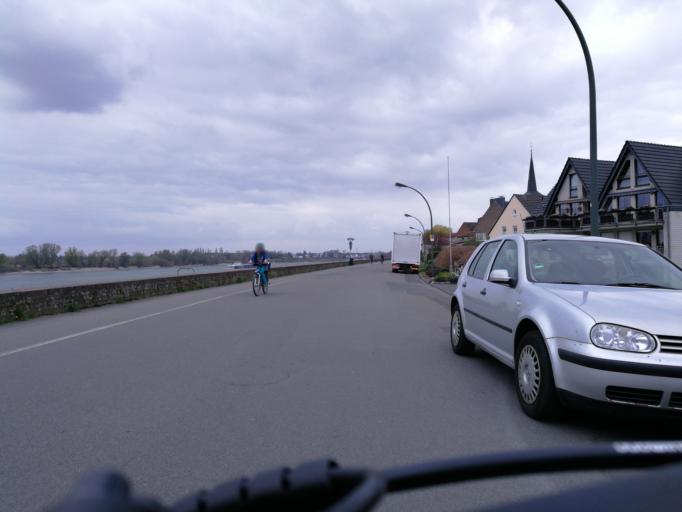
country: DE
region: North Rhine-Westphalia
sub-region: Regierungsbezirk Dusseldorf
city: Dusseldorf
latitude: 51.1853
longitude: 6.7672
